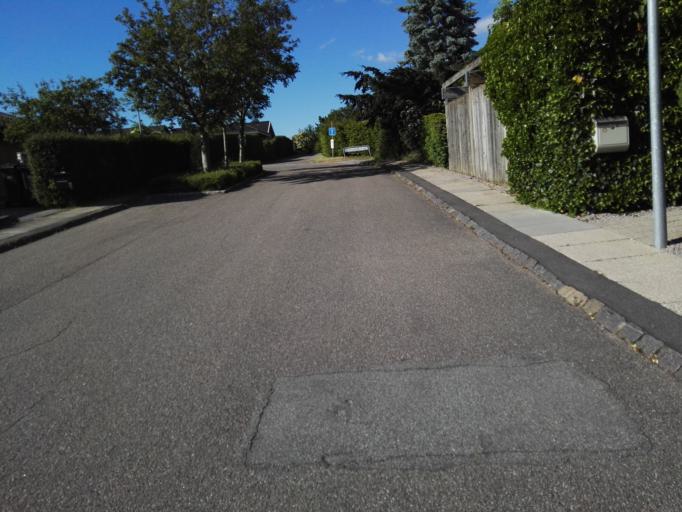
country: DK
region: Capital Region
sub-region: Egedal Kommune
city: Olstykke
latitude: 55.8025
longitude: 12.1624
